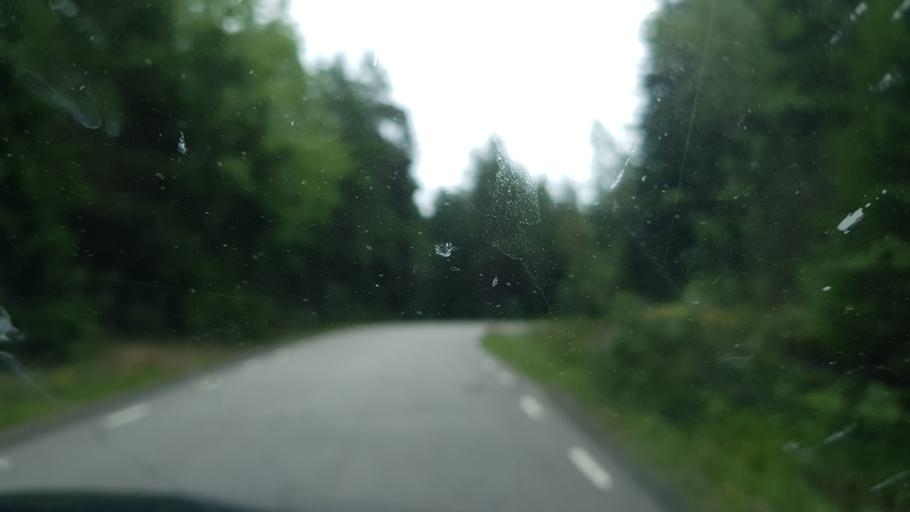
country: SE
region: Uppsala
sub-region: Osthammars Kommun
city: Oregrund
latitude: 60.3678
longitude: 18.4238
